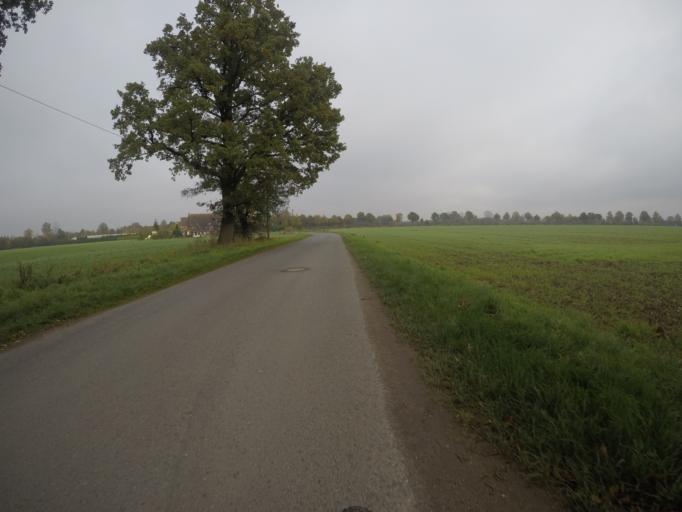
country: DE
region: North Rhine-Westphalia
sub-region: Regierungsbezirk Dusseldorf
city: Bocholt
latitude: 51.8241
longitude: 6.5753
